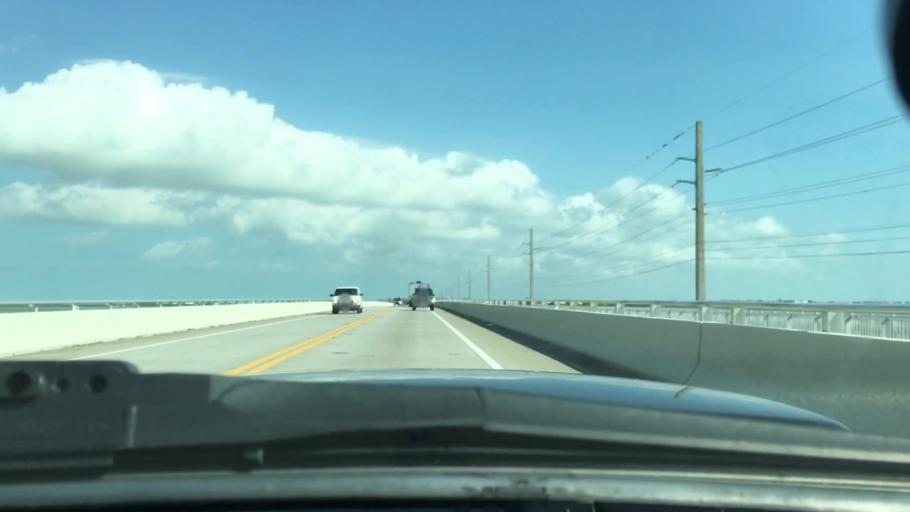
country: US
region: Florida
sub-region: Monroe County
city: Big Coppitt Key
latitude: 24.6318
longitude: -81.5887
